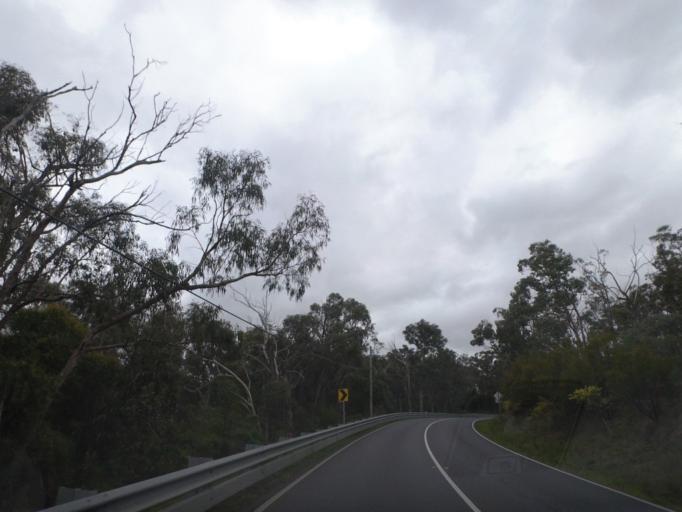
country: AU
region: Victoria
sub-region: Nillumbik
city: Diamond Creek
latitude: -37.6659
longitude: 145.1472
